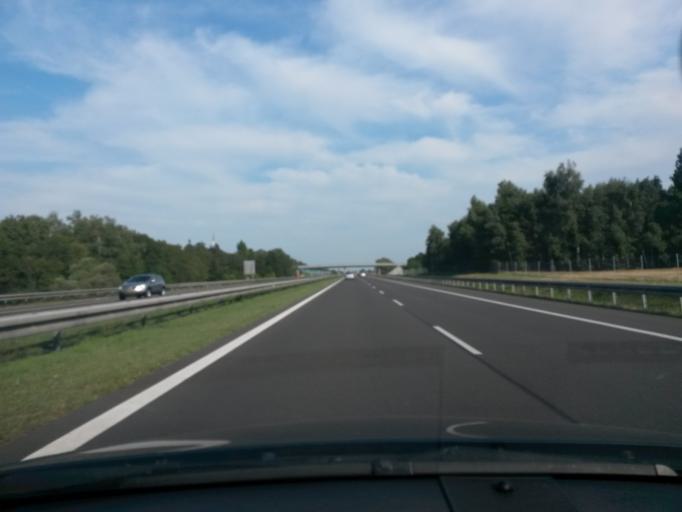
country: PL
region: Greater Poland Voivodeship
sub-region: Powiat slupecki
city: Slupca
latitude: 52.2451
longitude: 17.8605
